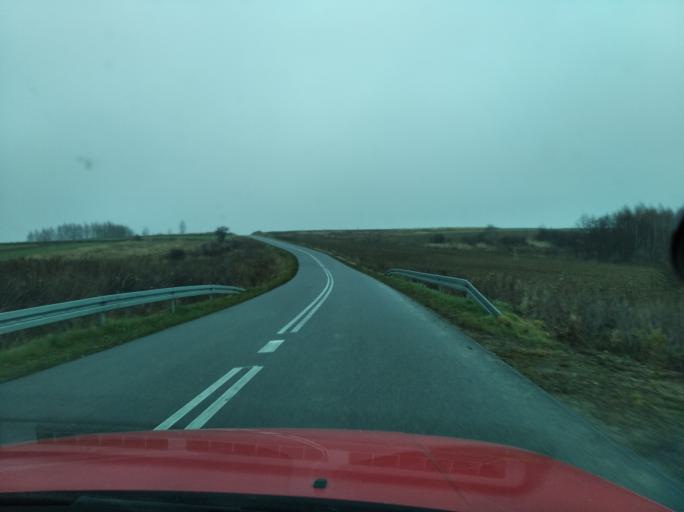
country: PL
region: Subcarpathian Voivodeship
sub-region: Powiat jaroslawski
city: Jodlowka
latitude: 49.8925
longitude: 22.4831
